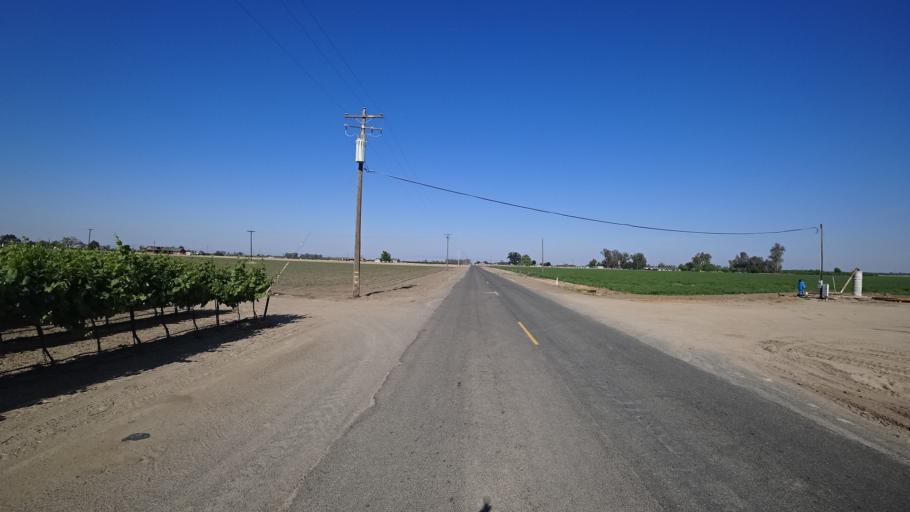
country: US
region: California
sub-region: Fresno County
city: Riverdale
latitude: 36.3658
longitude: -119.8558
